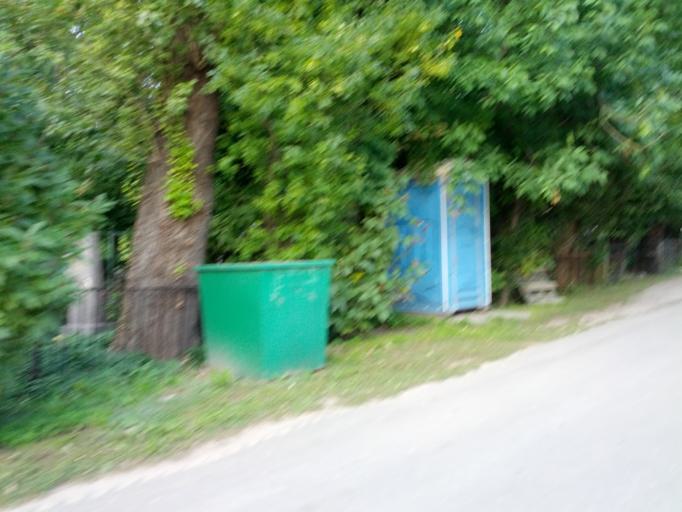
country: RU
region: St.-Petersburg
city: Krasnogvargeisky
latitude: 59.9507
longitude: 30.4399
